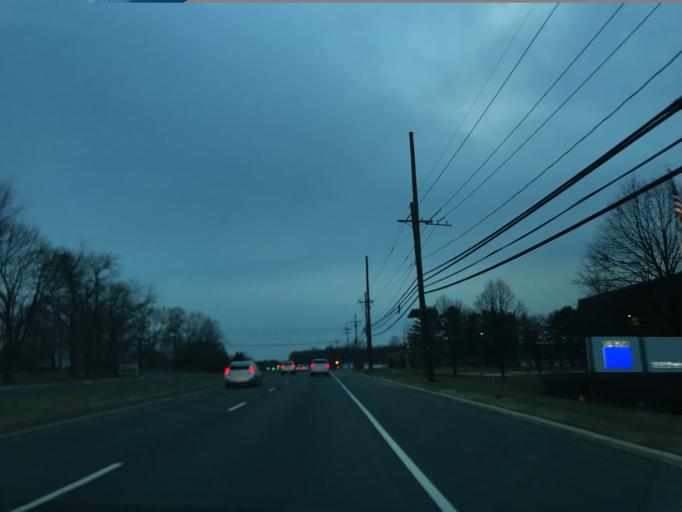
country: US
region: New Jersey
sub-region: Middlesex County
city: Cranbury
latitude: 40.3355
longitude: -74.5037
